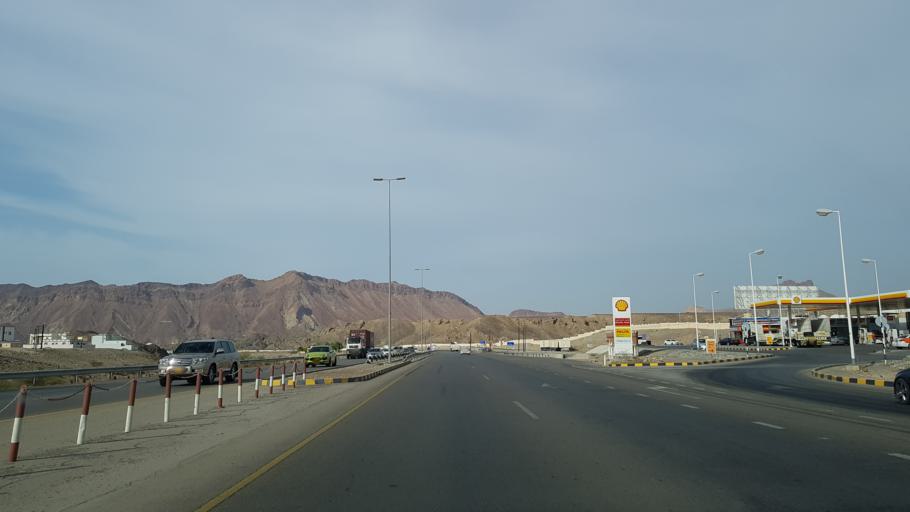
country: OM
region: Muhafazat ad Dakhiliyah
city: Bidbid
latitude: 23.4172
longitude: 58.1172
